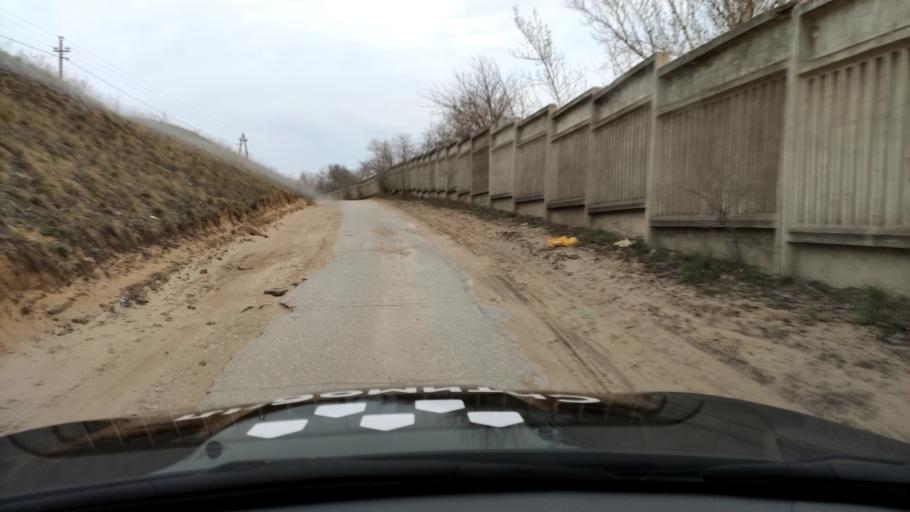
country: RU
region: Samara
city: Zhigulevsk
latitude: 53.4763
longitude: 49.5340
